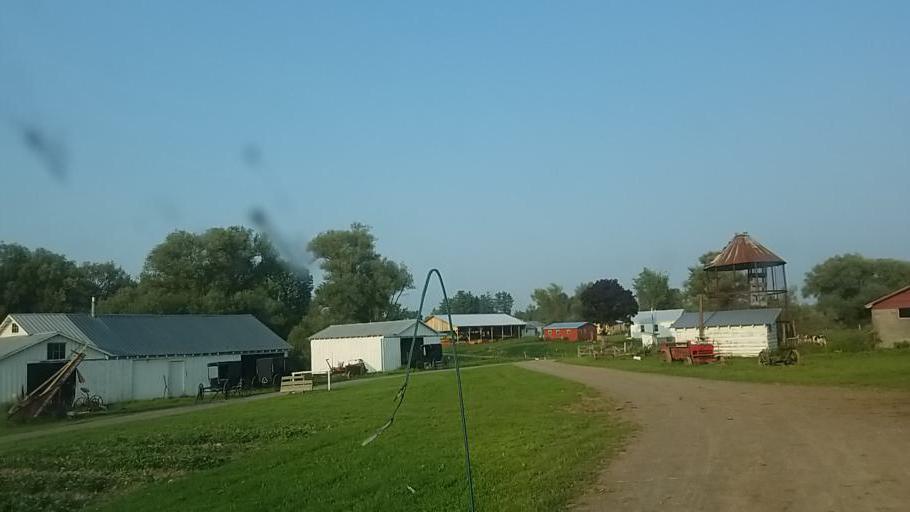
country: US
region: New York
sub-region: Montgomery County
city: Fonda
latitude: 42.9008
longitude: -74.4056
